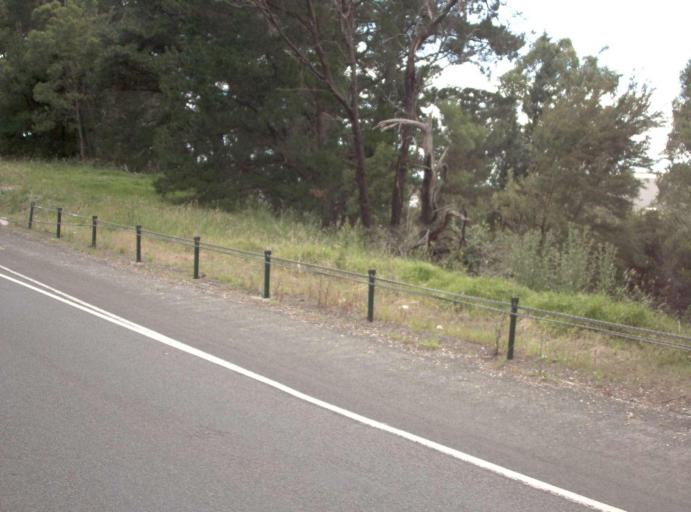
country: AU
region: Victoria
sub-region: Latrobe
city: Morwell
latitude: -38.1783
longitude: 146.4416
